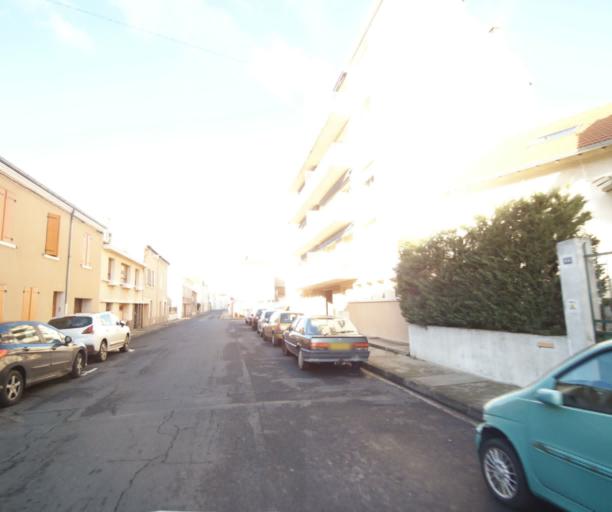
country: FR
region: Rhone-Alpes
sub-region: Departement de la Loire
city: Roanne
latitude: 46.0437
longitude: 4.0668
